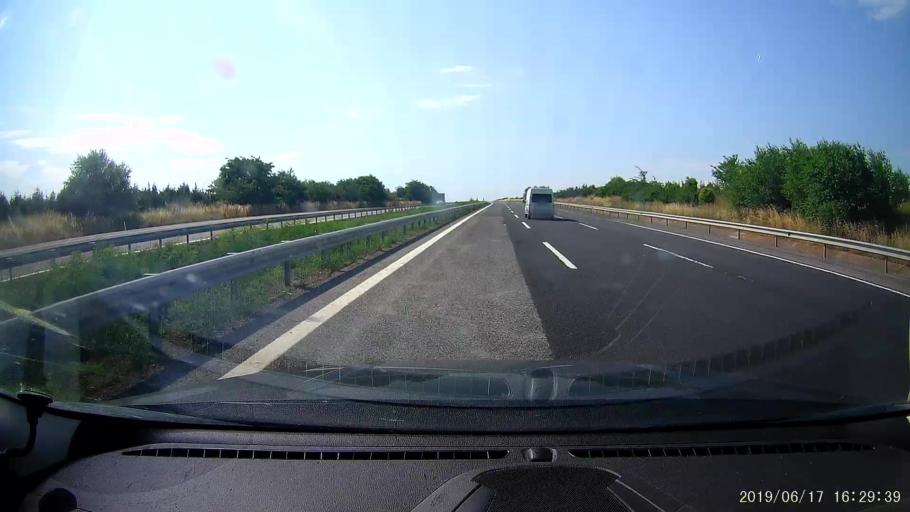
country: TR
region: Tekirdag
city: Beyazkoy
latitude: 41.3364
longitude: 27.6756
